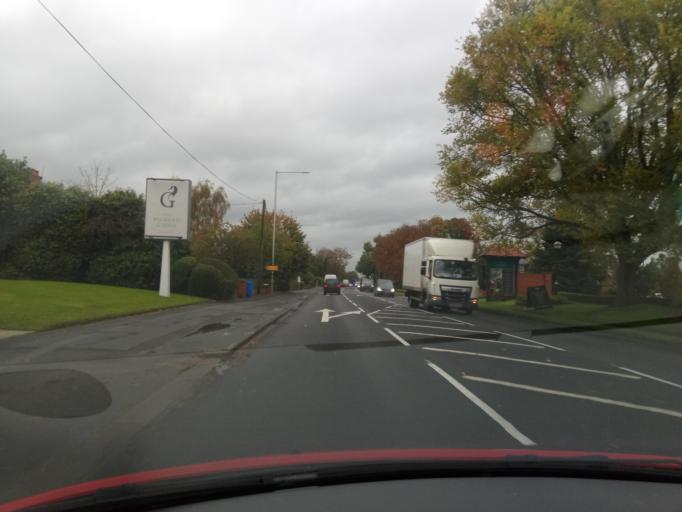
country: GB
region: England
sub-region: Lancashire
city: Catterall
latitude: 53.8302
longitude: -2.7377
